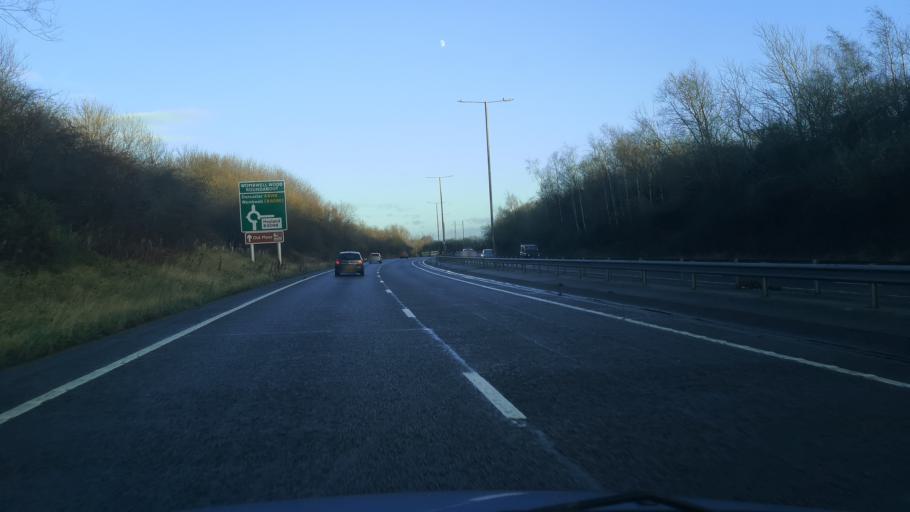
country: GB
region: England
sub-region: Barnsley
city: Hoyland Nether
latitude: 53.5118
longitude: -1.4390
